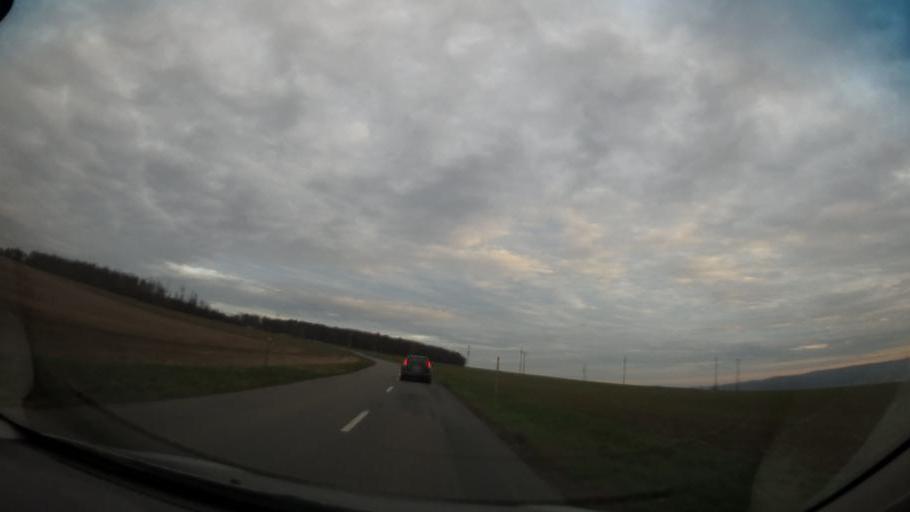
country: CZ
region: South Moravian
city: Zbysov
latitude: 49.1315
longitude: 16.3638
